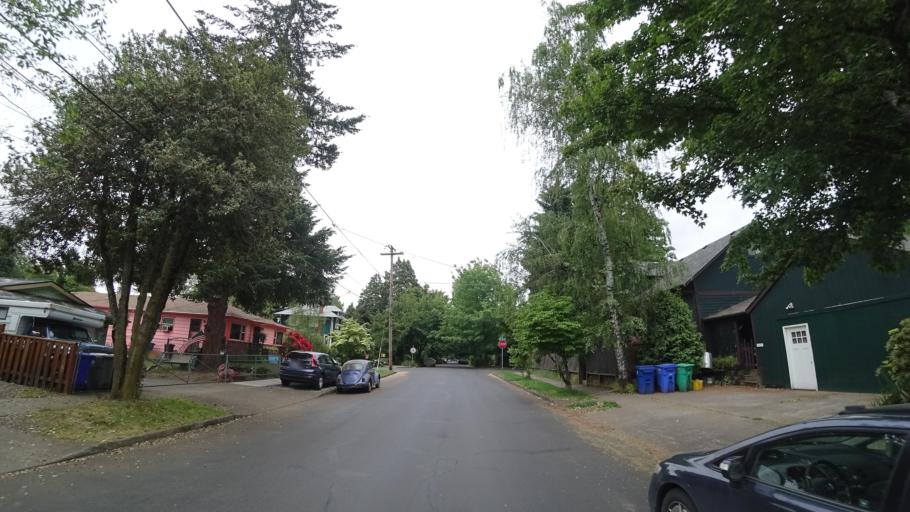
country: US
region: Oregon
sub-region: Multnomah County
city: Portland
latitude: 45.5012
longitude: -122.6280
